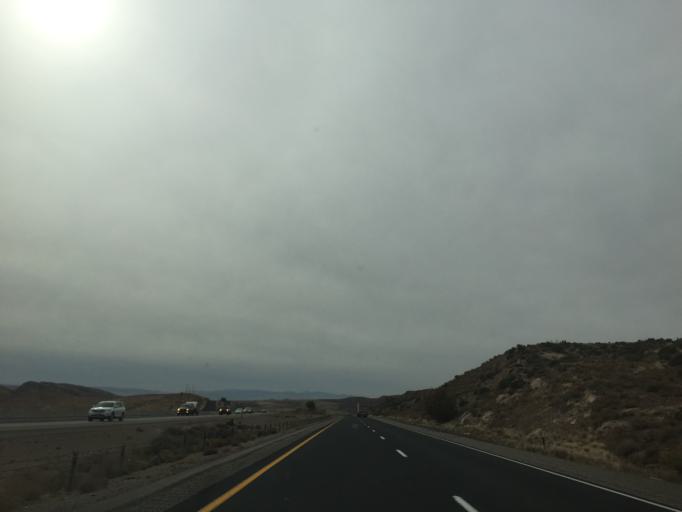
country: US
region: Utah
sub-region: Washington County
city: Toquerville
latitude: 37.2228
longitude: -113.3822
